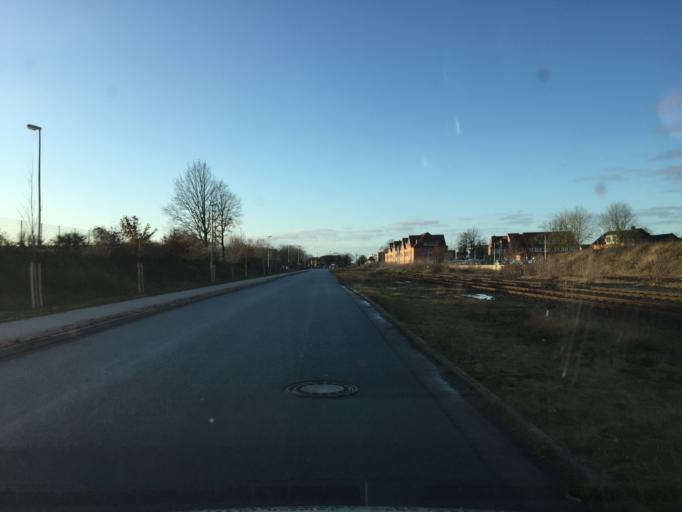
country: DE
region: Lower Saxony
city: Sulingen
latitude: 52.6872
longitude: 8.8139
